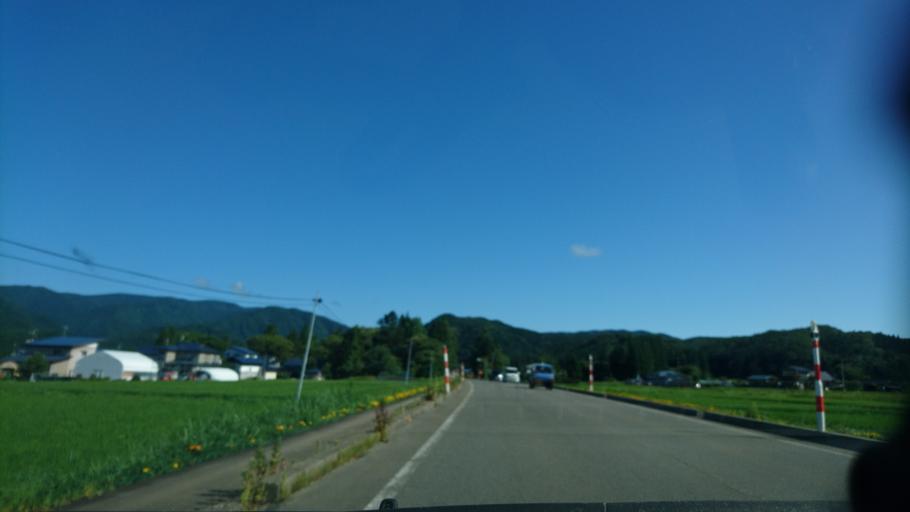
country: JP
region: Akita
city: Kakunodatemachi
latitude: 39.6662
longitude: 140.5687
